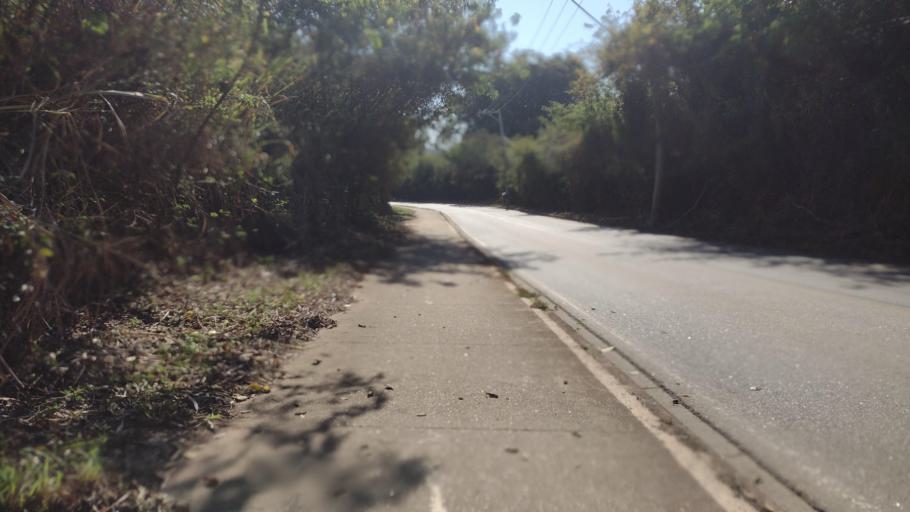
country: BR
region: Sao Paulo
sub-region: Sorocaba
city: Sorocaba
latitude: -23.4099
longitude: -47.4778
